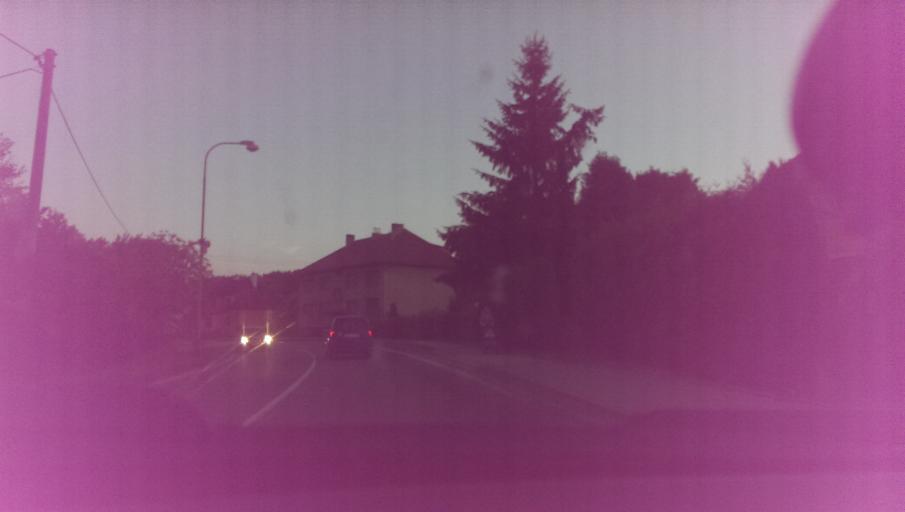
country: CZ
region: Zlin
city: Valasska Polanka
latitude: 49.2676
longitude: 17.9959
